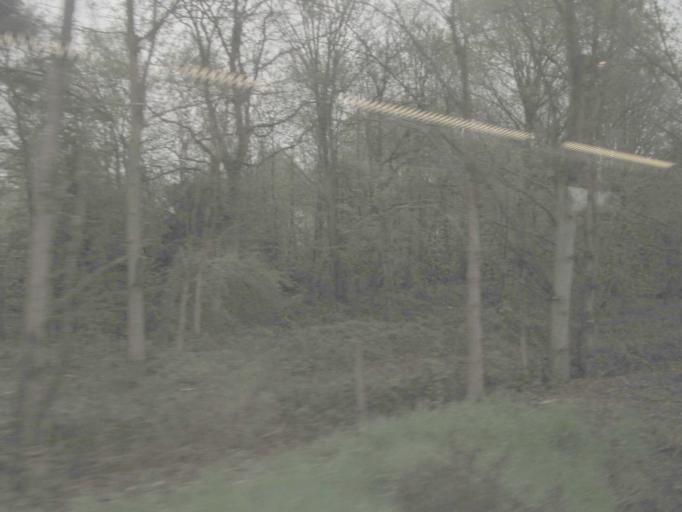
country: GB
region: England
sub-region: Bracknell Forest
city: Sandhurst
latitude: 51.3292
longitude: -0.7742
